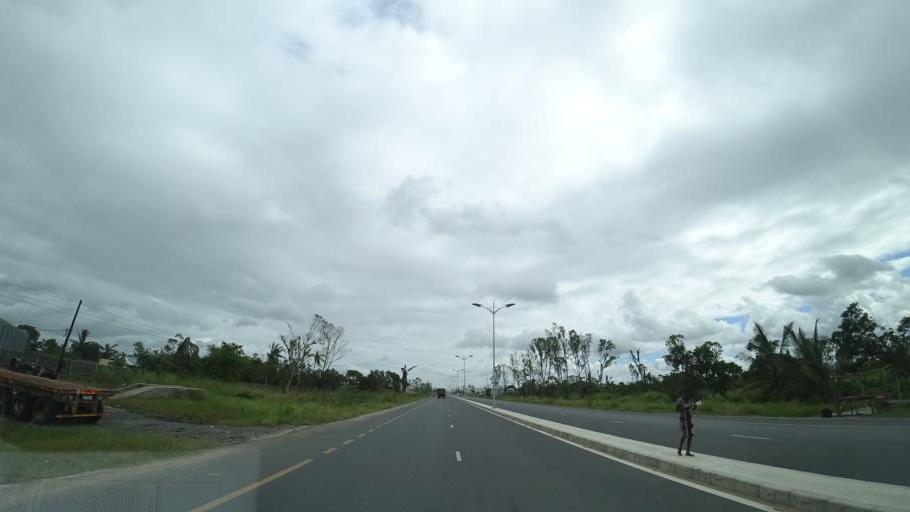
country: MZ
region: Sofala
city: Dondo
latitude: -19.7095
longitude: 34.7951
